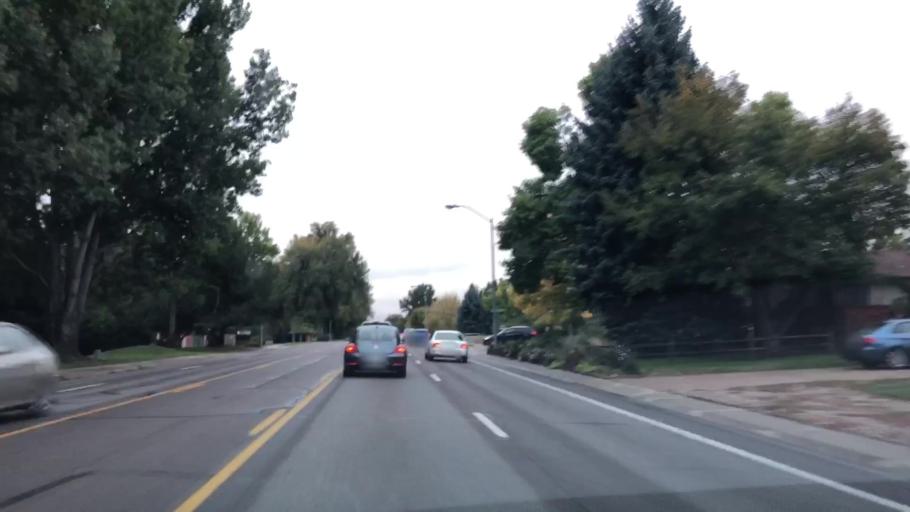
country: US
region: Colorado
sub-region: Larimer County
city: Fort Collins
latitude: 40.5605
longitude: -105.0580
